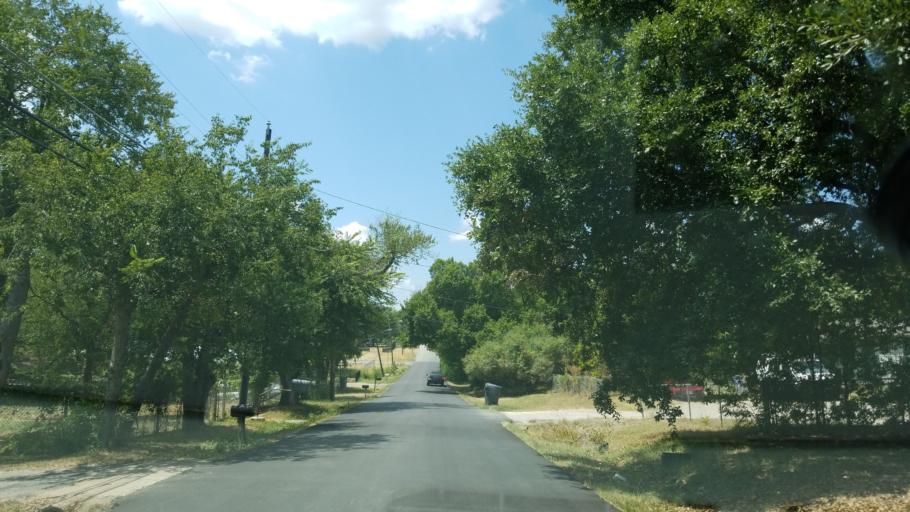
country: US
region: Texas
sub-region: Dallas County
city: Cockrell Hill
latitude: 32.7138
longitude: -96.9029
